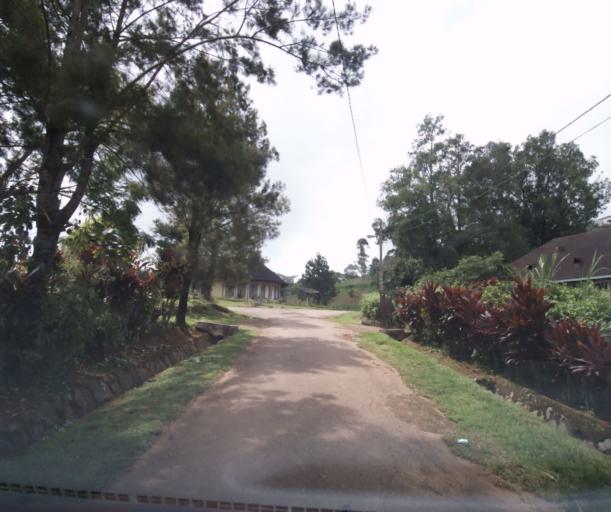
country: CM
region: West
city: Dschang
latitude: 5.4412
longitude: 10.0676
